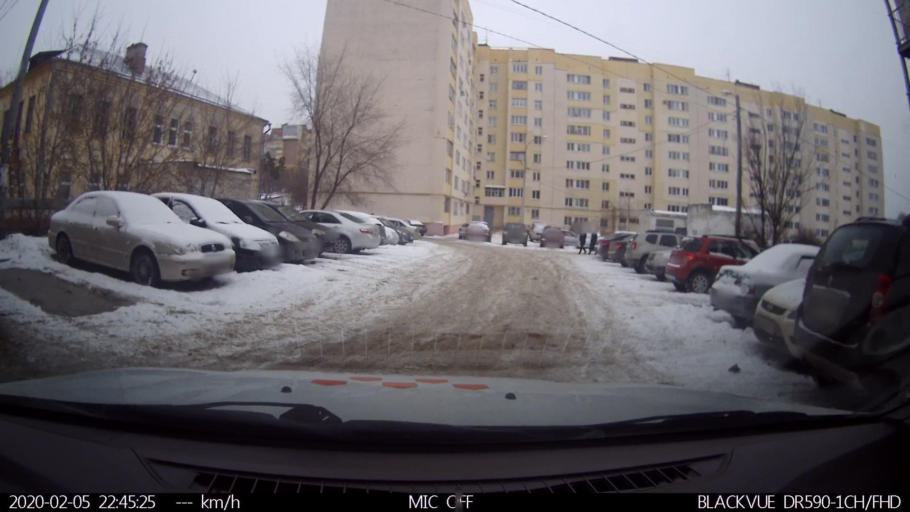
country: RU
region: Nizjnij Novgorod
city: Imeni Stepana Razina
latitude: 54.7047
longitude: 44.4122
